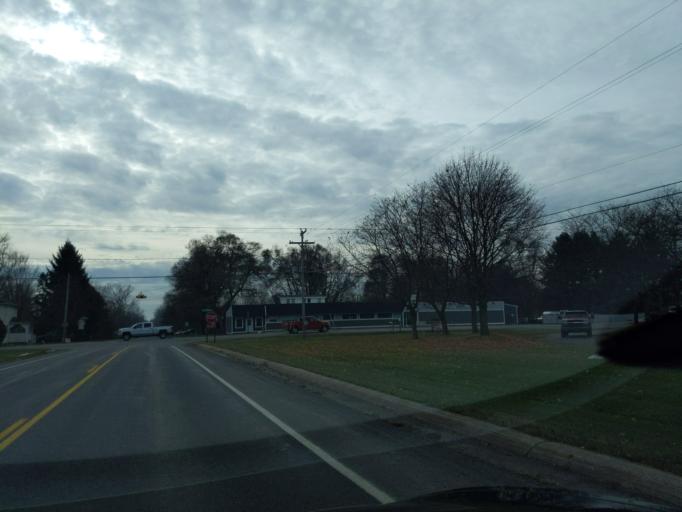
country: US
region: Michigan
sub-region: Ingham County
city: Holt
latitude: 42.5827
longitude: -84.5229
